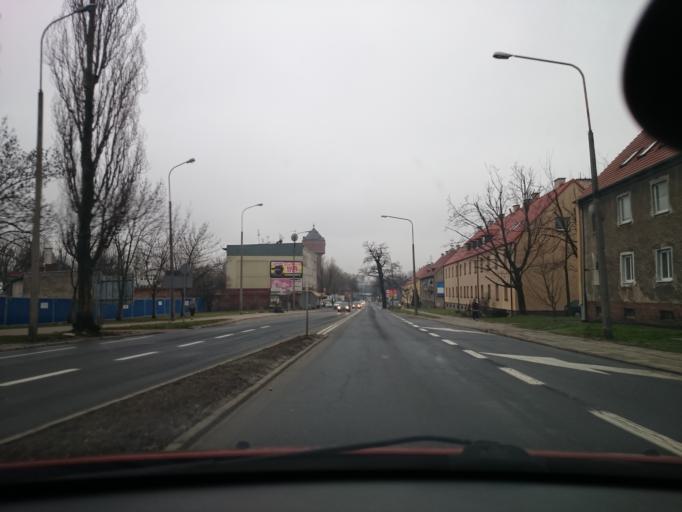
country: PL
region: Opole Voivodeship
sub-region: Powiat opolski
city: Opole
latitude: 50.6783
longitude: 17.9367
